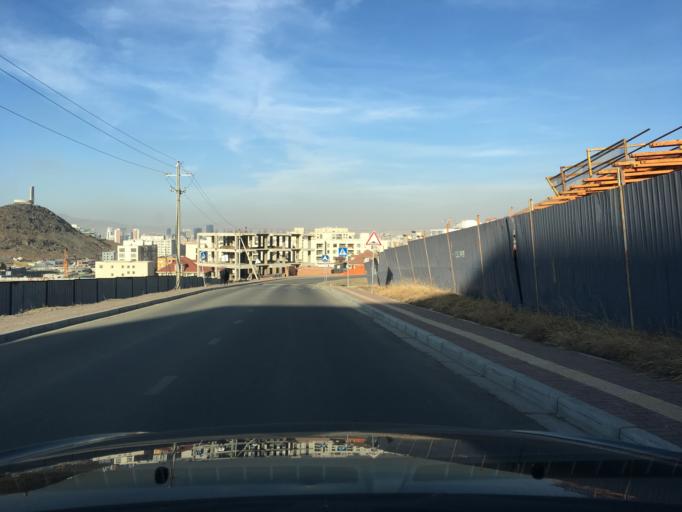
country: MN
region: Ulaanbaatar
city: Ulaanbaatar
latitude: 47.8767
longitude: 106.9175
